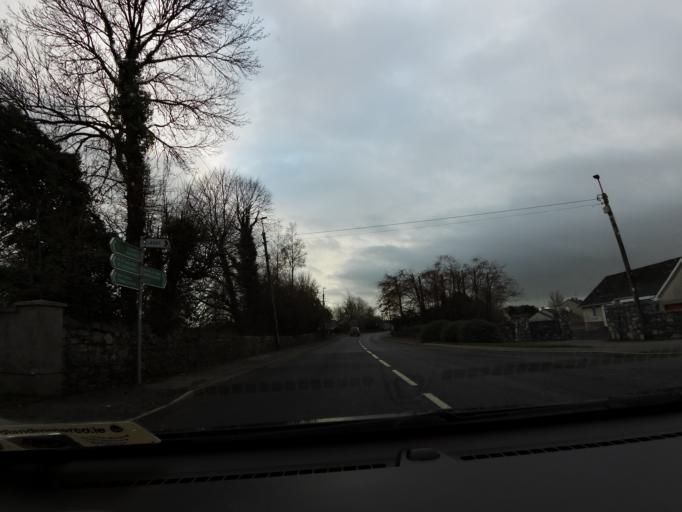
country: IE
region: Connaught
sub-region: County Galway
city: Portumna
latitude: 53.0955
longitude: -8.2129
